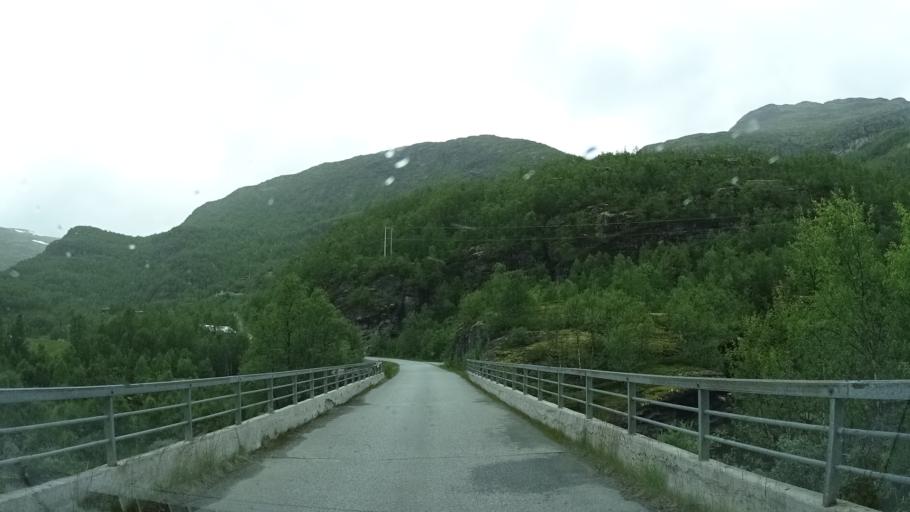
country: NO
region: Sogn og Fjordane
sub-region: Laerdal
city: Laerdalsoyri
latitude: 60.8252
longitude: 7.5198
